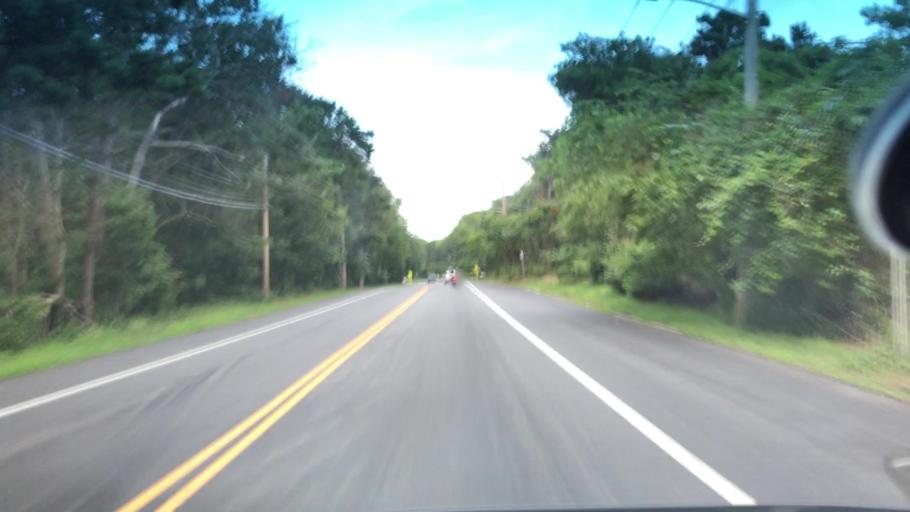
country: US
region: New York
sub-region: Suffolk County
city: East Shoreham
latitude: 40.9435
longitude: -72.8694
